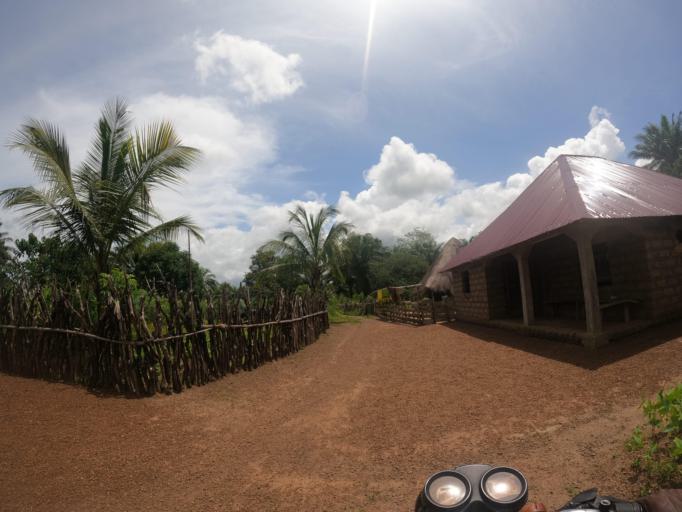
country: SL
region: Northern Province
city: Makeni
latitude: 9.1219
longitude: -12.2595
